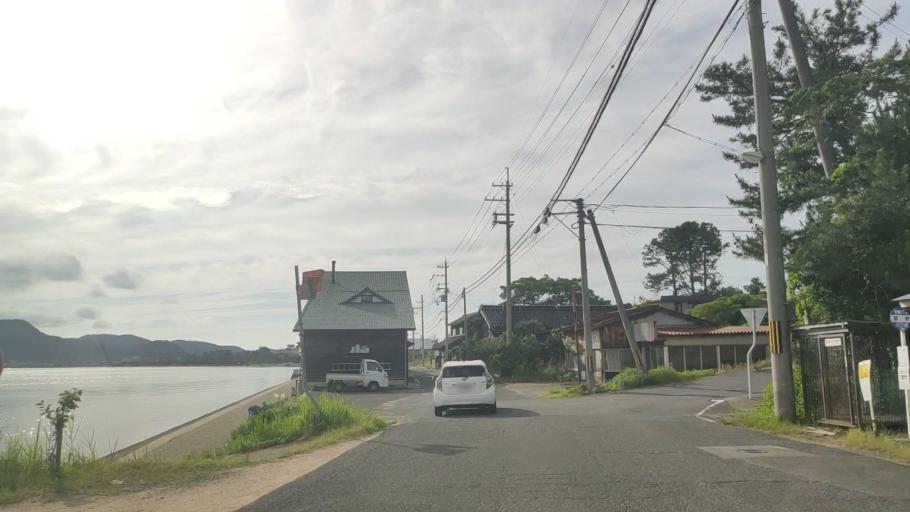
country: JP
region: Hyogo
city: Toyooka
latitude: 35.6391
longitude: 134.9253
